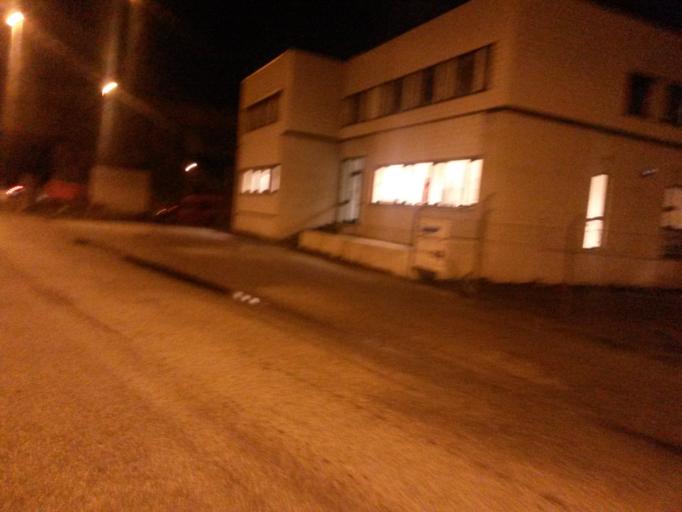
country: NO
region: Rogaland
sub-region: Stavanger
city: Stavanger
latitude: 58.9560
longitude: 5.7451
